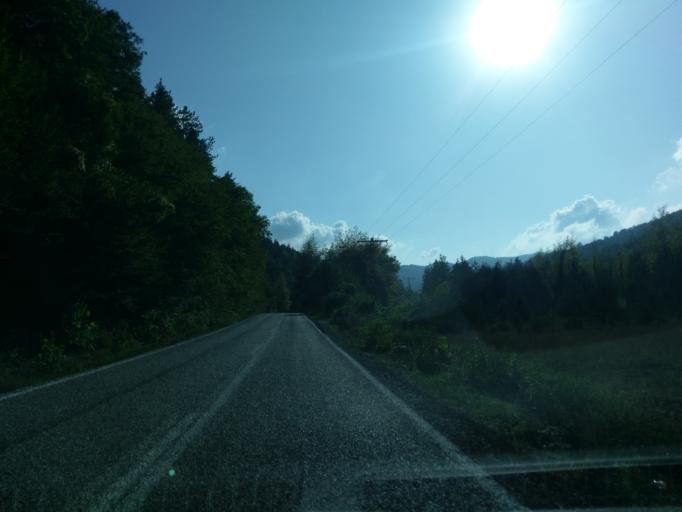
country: TR
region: Sinop
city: Yenikonak
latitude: 41.8842
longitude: 34.5646
